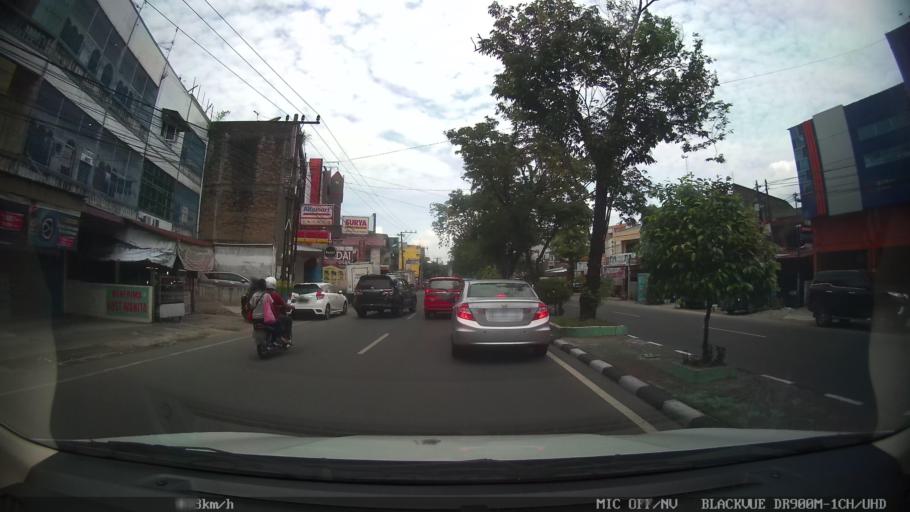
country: ID
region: North Sumatra
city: Medan
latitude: 3.5526
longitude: 98.6603
